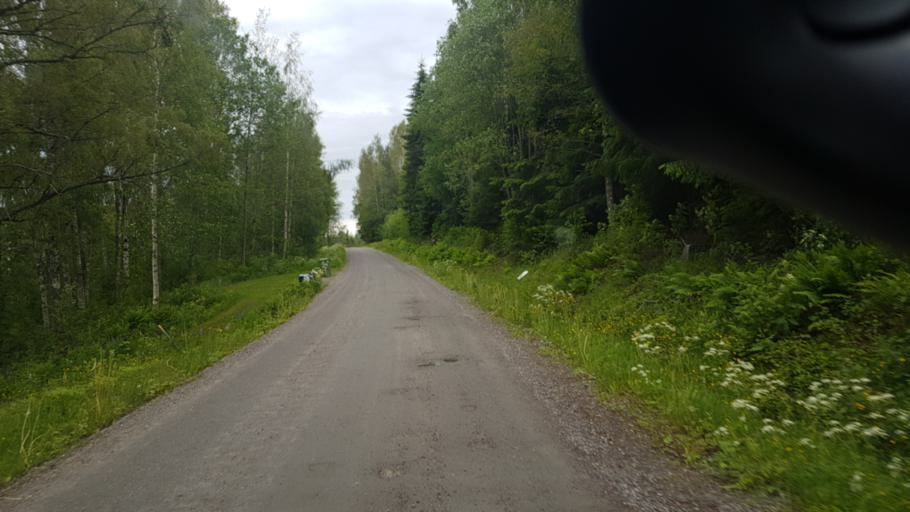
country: SE
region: Vaermland
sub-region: Eda Kommun
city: Amotfors
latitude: 59.7383
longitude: 12.2778
